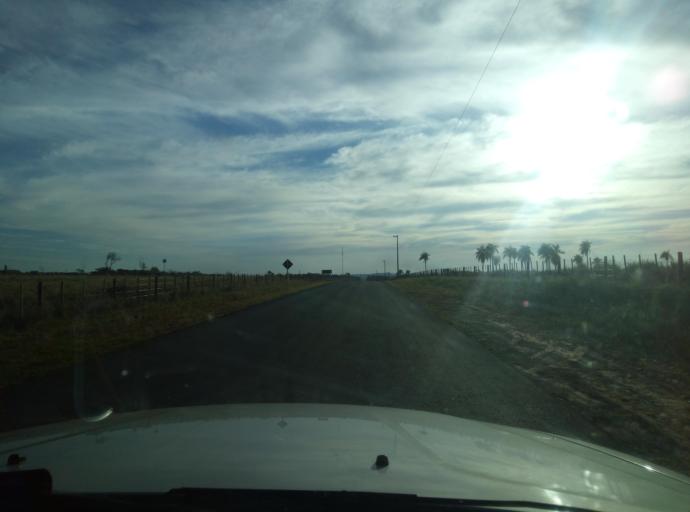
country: PY
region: Caaguazu
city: Carayao
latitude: -25.1551
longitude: -56.3126
